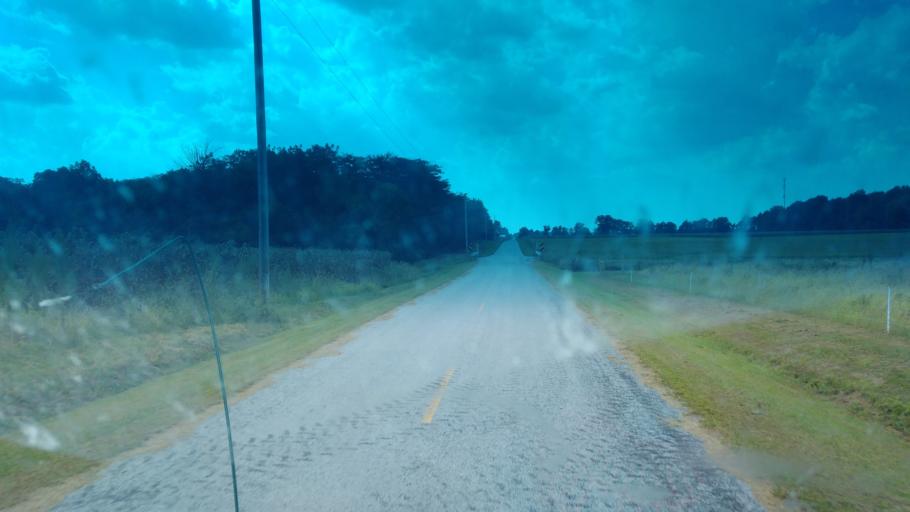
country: US
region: Ohio
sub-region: Hardin County
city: Kenton
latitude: 40.7176
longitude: -83.5974
